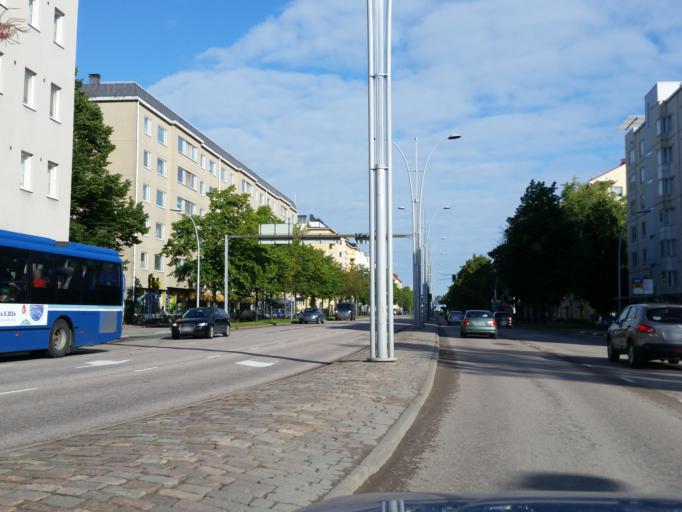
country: FI
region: Uusimaa
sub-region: Helsinki
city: Teekkarikylae
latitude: 60.1969
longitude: 24.8848
